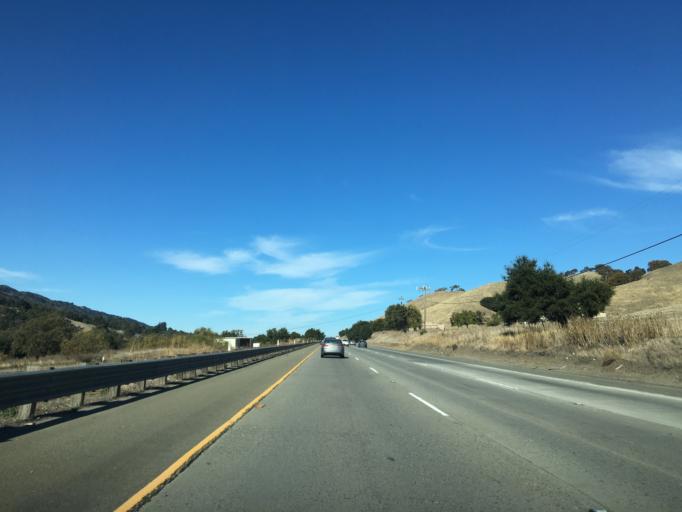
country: US
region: California
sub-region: Alameda County
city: Pleasanton
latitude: 37.6143
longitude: -121.8761
